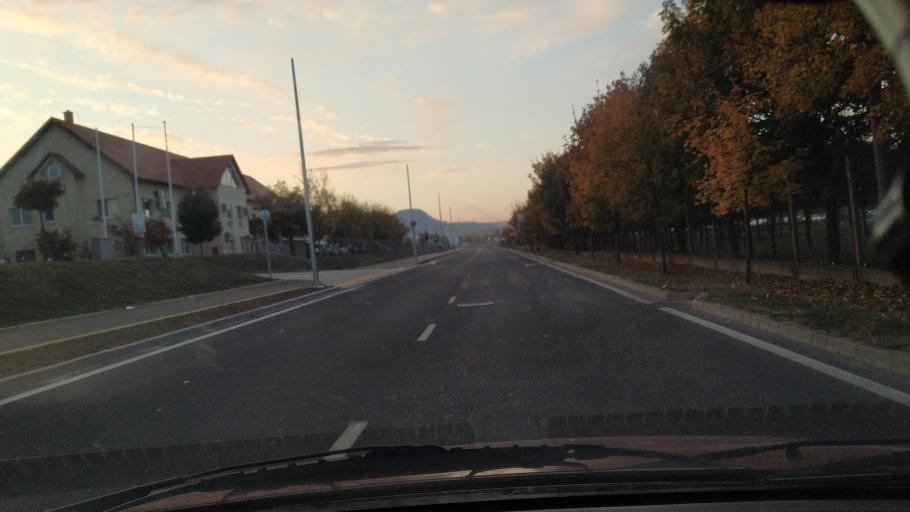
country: HU
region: Komarom-Esztergom
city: Esztergom
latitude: 47.7690
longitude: 18.7543
